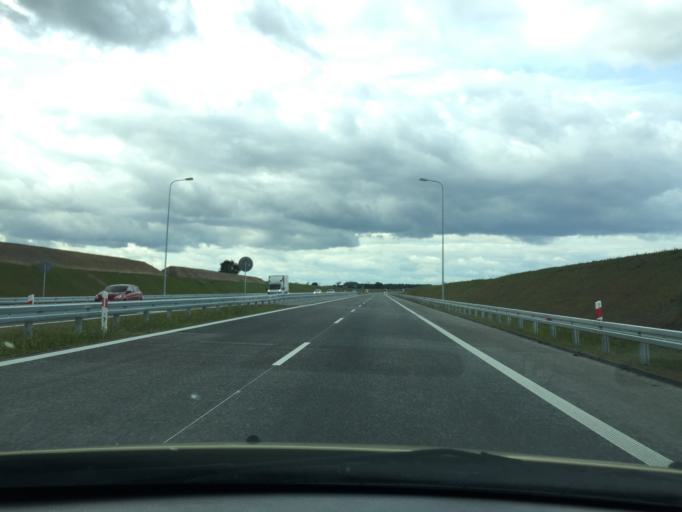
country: PL
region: Greater Poland Voivodeship
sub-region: Powiat jarocinski
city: Jarocin
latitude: 51.9823
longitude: 17.5185
